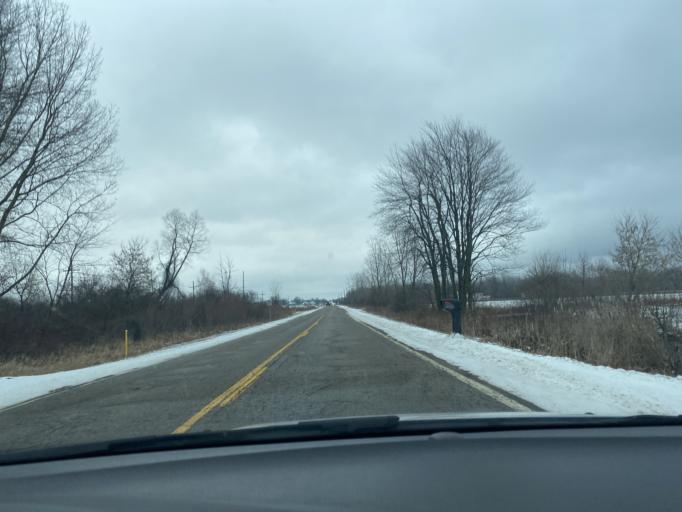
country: US
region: Michigan
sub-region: Lapeer County
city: North Branch
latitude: 43.2078
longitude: -83.1884
